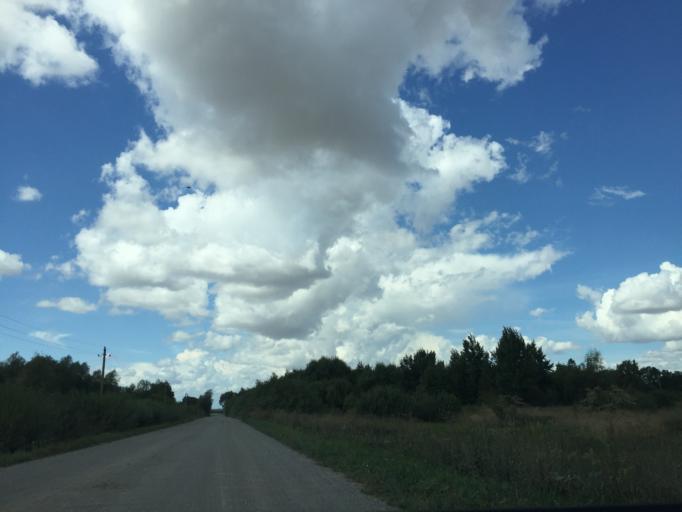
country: LV
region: Rundales
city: Pilsrundale
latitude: 56.3001
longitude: 23.9942
